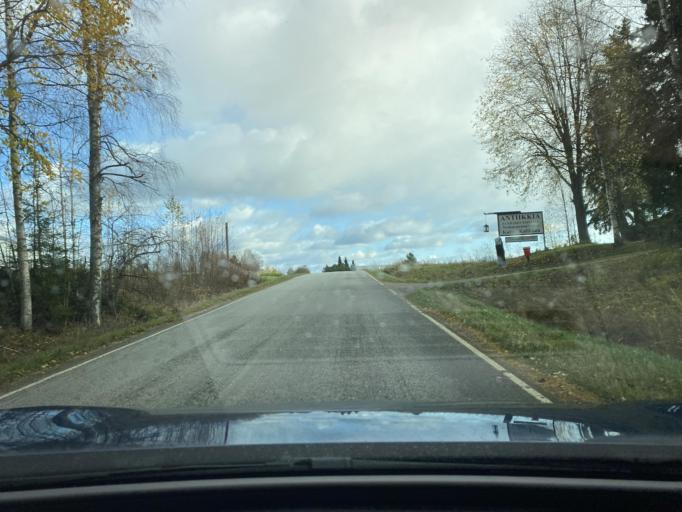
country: FI
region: Varsinais-Suomi
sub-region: Loimaa
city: Aura
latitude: 60.7028
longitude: 22.6018
